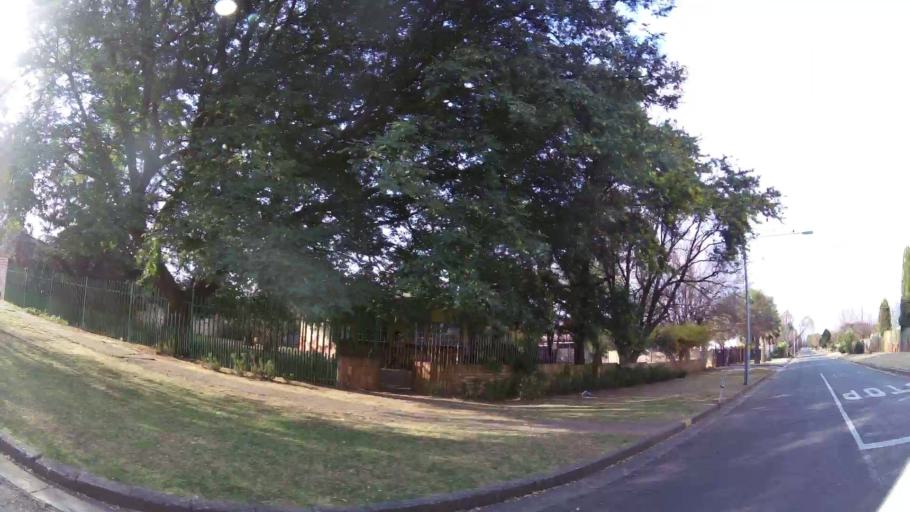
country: ZA
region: Gauteng
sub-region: Ekurhuleni Metropolitan Municipality
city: Springs
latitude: -26.2772
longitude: 28.4467
